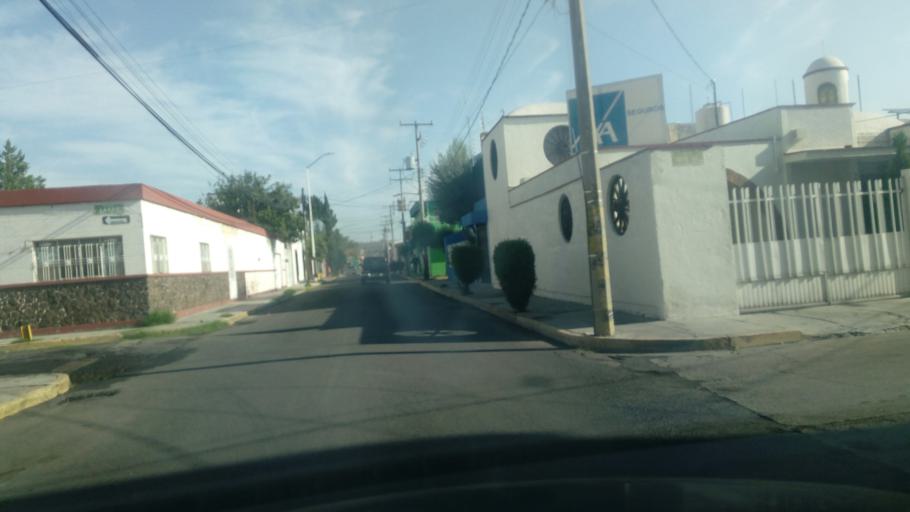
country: MX
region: Durango
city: Victoria de Durango
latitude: 24.0292
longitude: -104.6641
